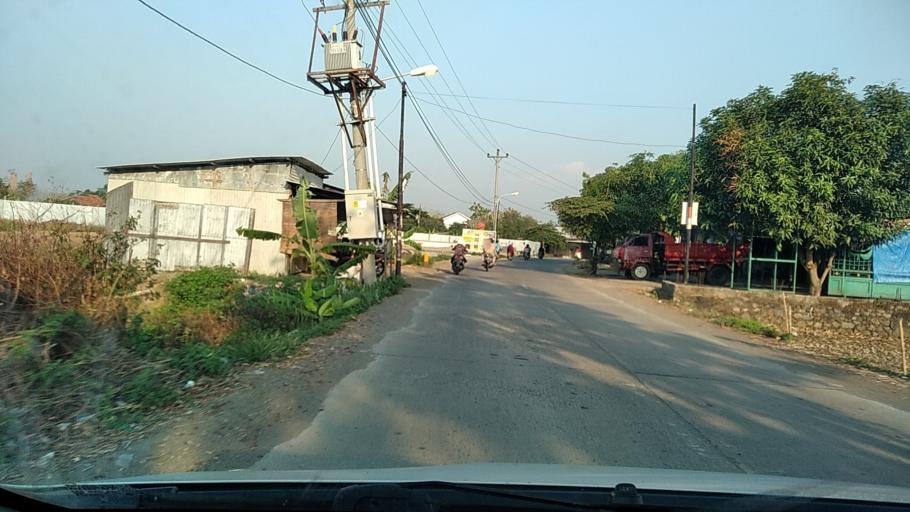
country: ID
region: Central Java
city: Mranggen
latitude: -7.0594
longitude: 110.4749
